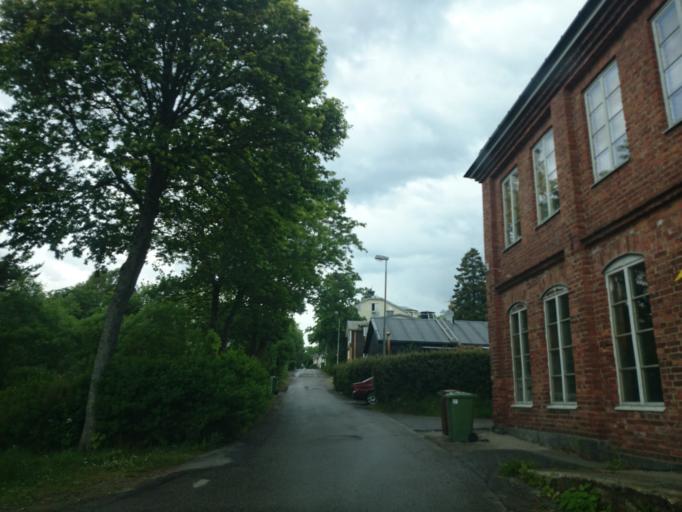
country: SE
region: Vaesternorrland
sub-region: Haernoesands Kommun
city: Haernoesand
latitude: 62.6234
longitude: 17.9282
